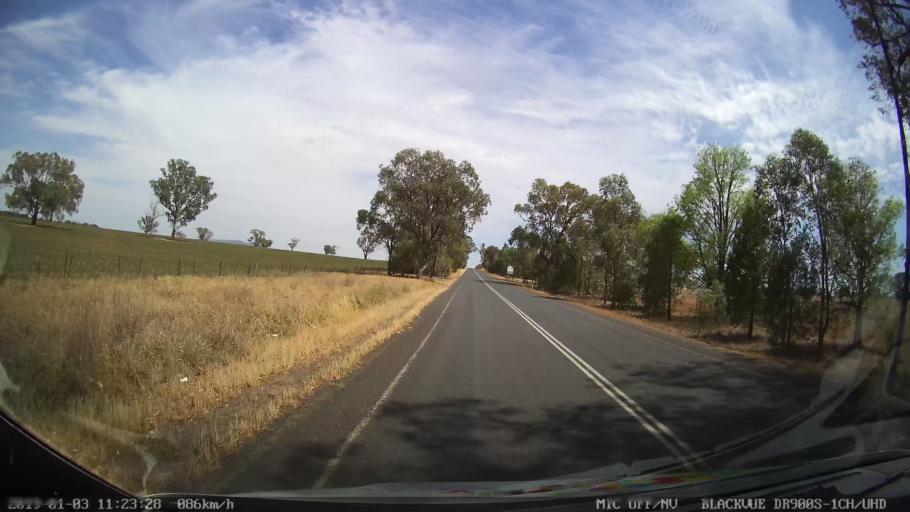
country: AU
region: New South Wales
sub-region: Weddin
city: Grenfell
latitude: -34.0627
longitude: 148.2426
